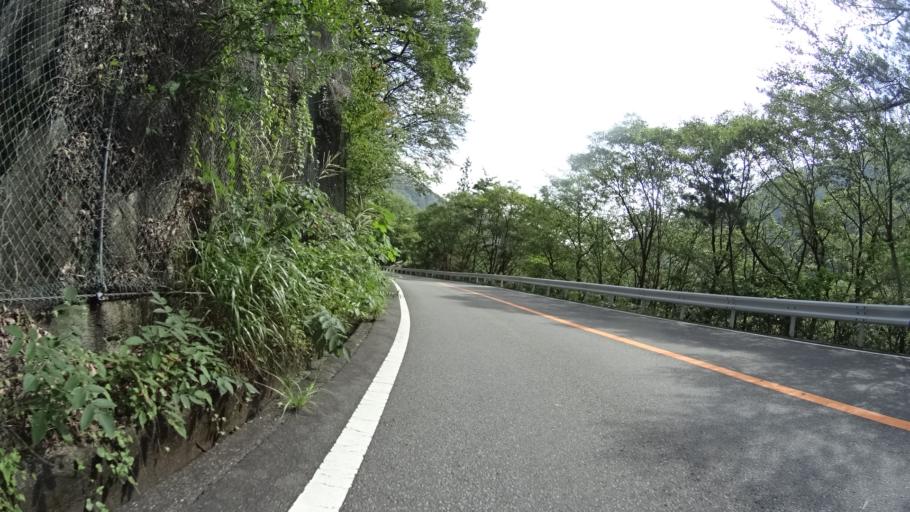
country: JP
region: Yamanashi
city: Kofu-shi
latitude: 35.7443
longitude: 138.5667
